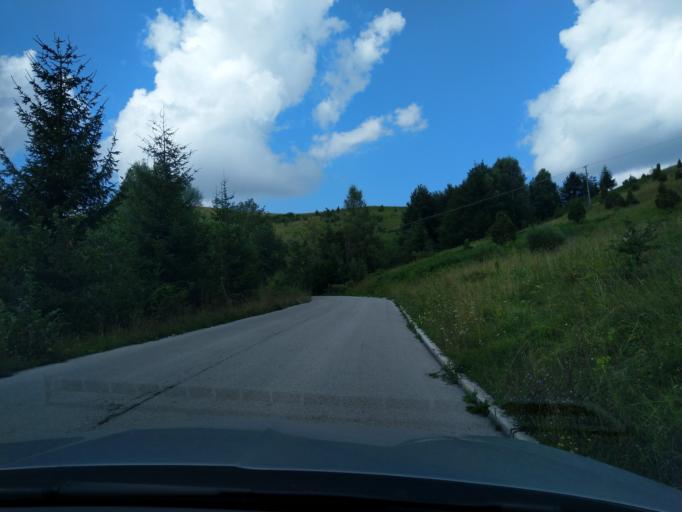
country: RS
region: Central Serbia
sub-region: Zlatiborski Okrug
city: Nova Varos
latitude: 43.5568
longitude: 19.9030
